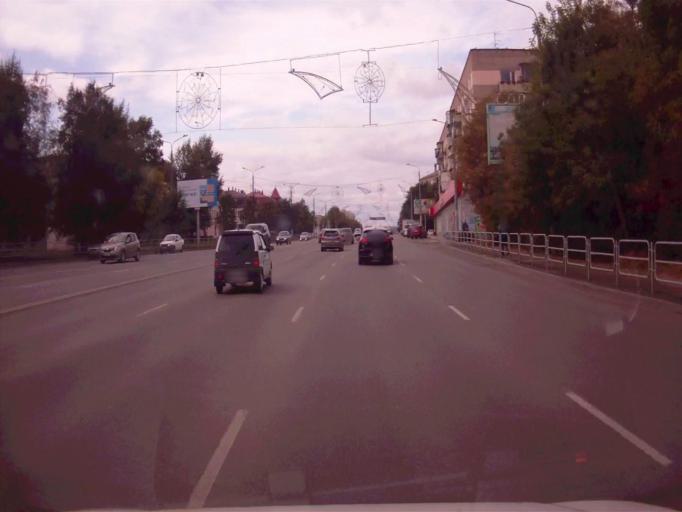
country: RU
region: Chelyabinsk
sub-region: Gorod Chelyabinsk
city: Chelyabinsk
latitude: 55.1385
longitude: 61.4003
